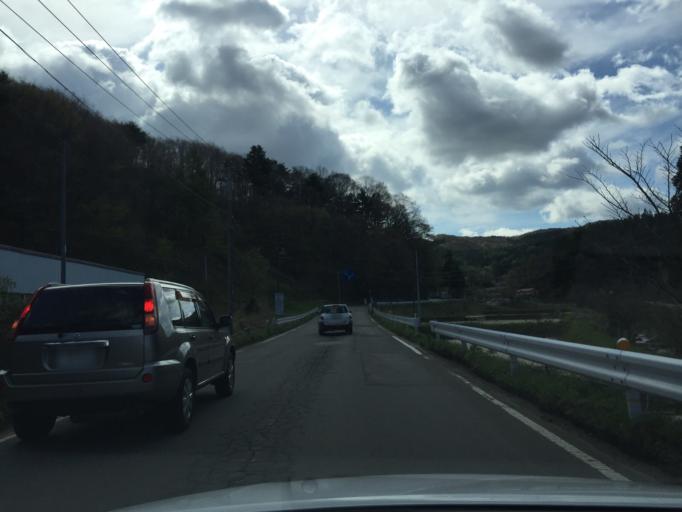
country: JP
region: Fukushima
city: Funehikimachi-funehiki
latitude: 37.5876
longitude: 140.6904
